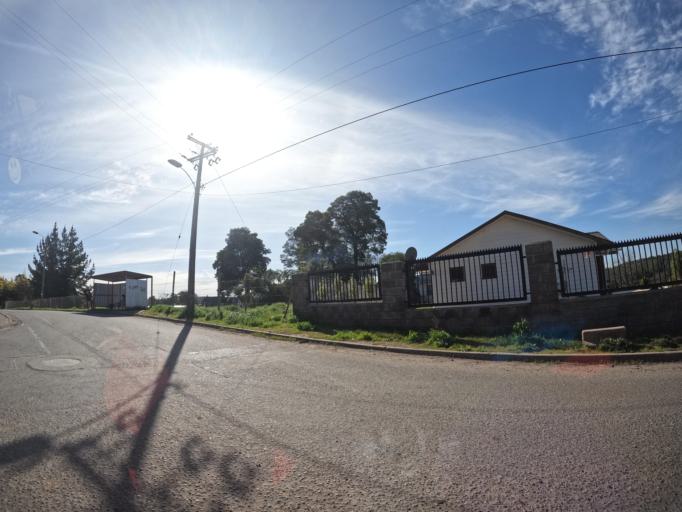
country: CL
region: Biobio
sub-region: Provincia de Concepcion
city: Chiguayante
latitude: -36.8968
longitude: -72.8056
